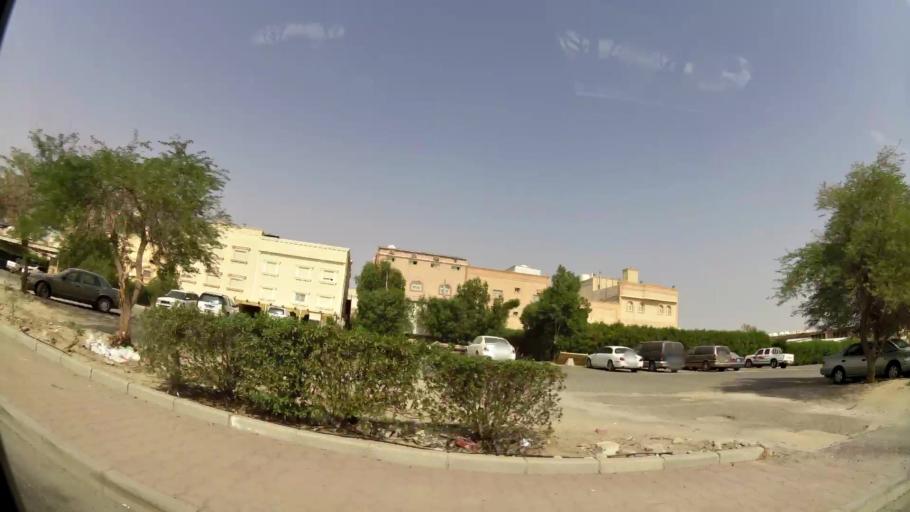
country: KW
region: Muhafazat al Jahra'
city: Al Jahra'
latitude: 29.3226
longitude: 47.6506
